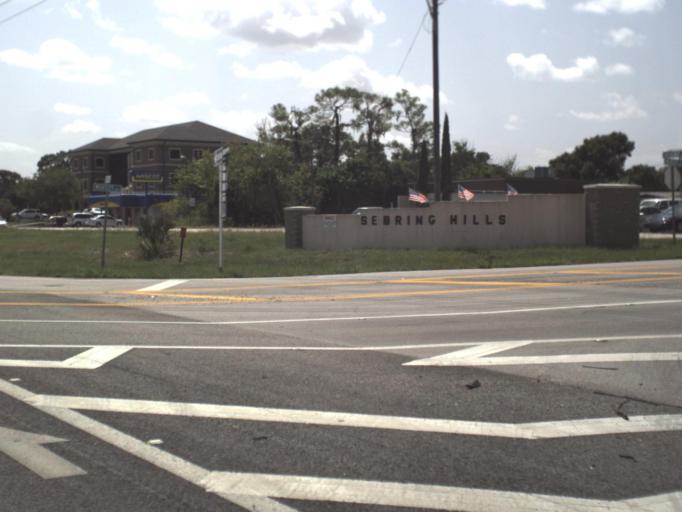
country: US
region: Florida
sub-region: Highlands County
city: Sebring
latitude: 27.4952
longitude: -81.4869
